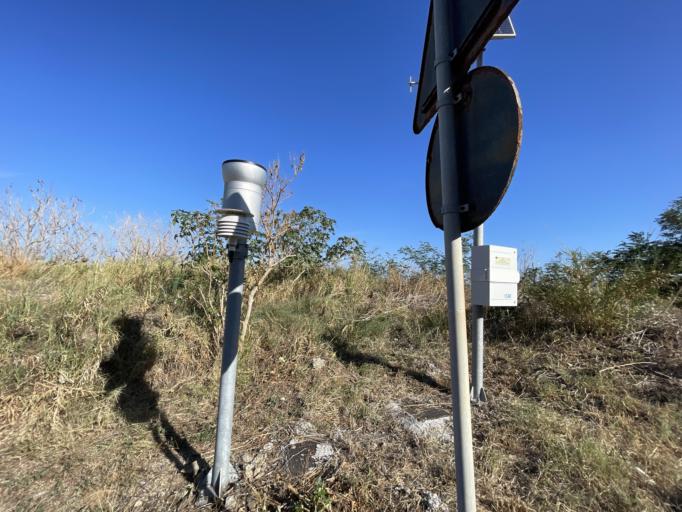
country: IT
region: Sicily
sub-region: Messina
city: Sparta'
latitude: 38.2908
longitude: 15.5116
